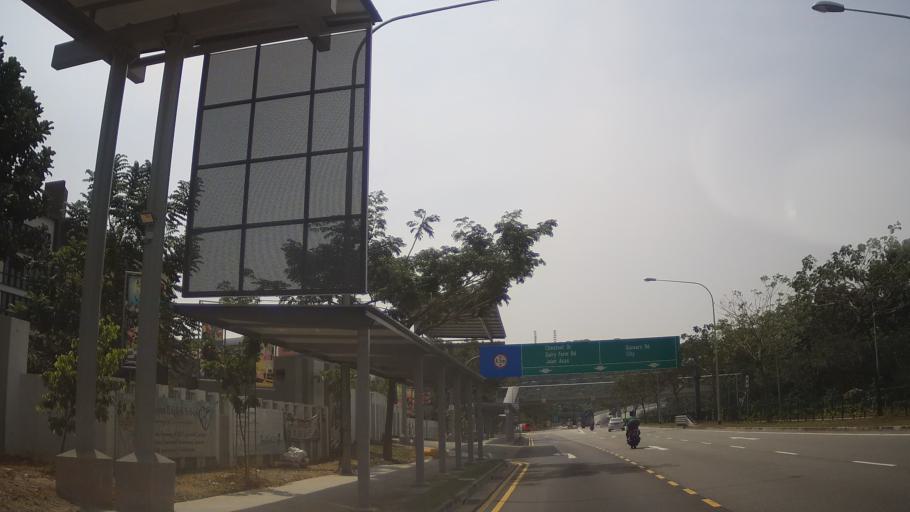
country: MY
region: Johor
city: Johor Bahru
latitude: 1.3681
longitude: 103.7655
